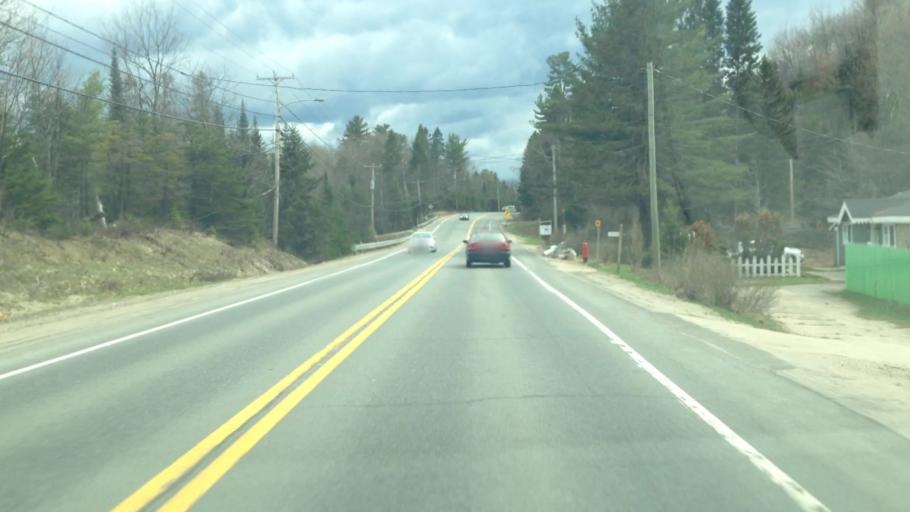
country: CA
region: Quebec
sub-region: Laurentides
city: Sainte-Adele
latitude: 45.9991
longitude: -74.1116
